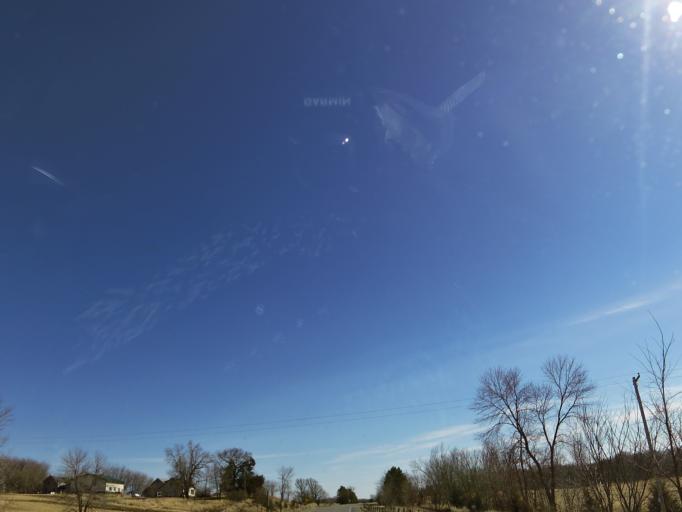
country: US
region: Minnesota
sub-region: Wright County
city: Rockford
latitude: 45.1104
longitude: -93.7835
